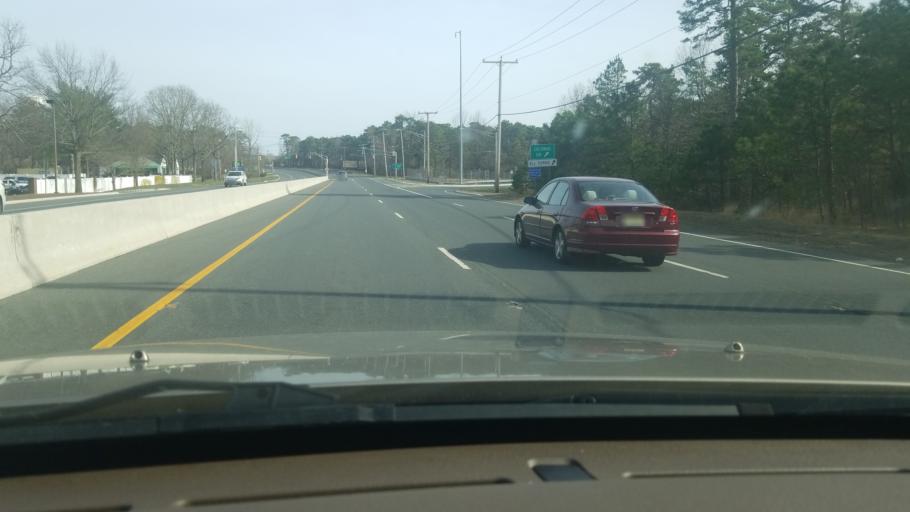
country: US
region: New Jersey
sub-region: Ocean County
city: Leisure Knoll
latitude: 40.0069
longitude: -74.2987
